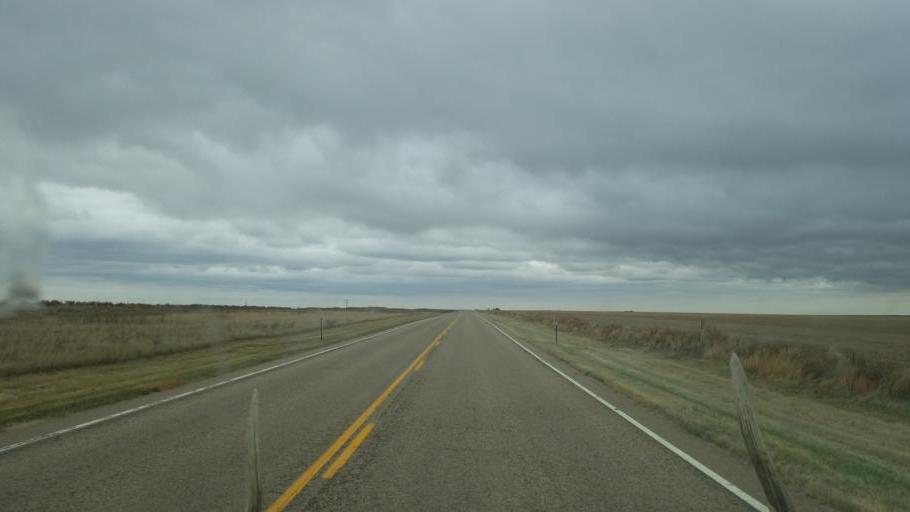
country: US
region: Colorado
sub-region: Cheyenne County
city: Cheyenne Wells
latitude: 38.8168
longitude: -102.5162
